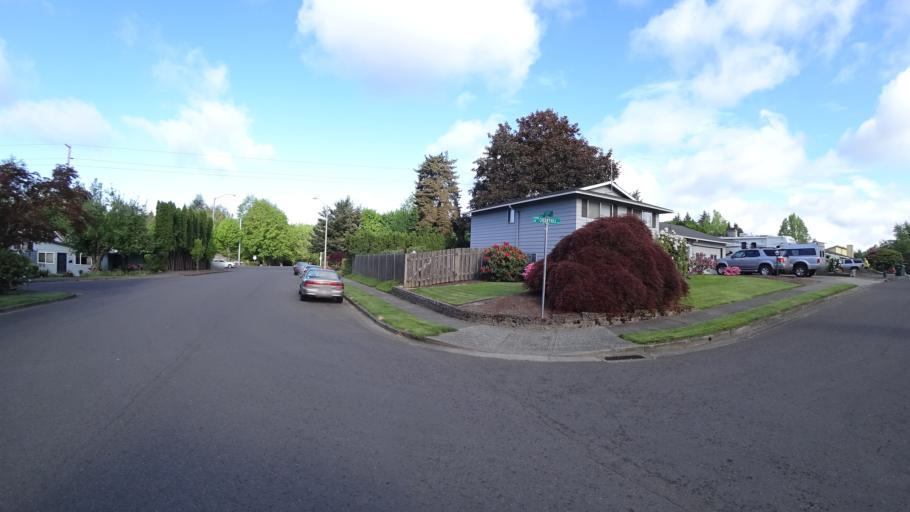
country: US
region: Oregon
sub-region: Washington County
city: Beaverton
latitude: 45.4721
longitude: -122.8251
